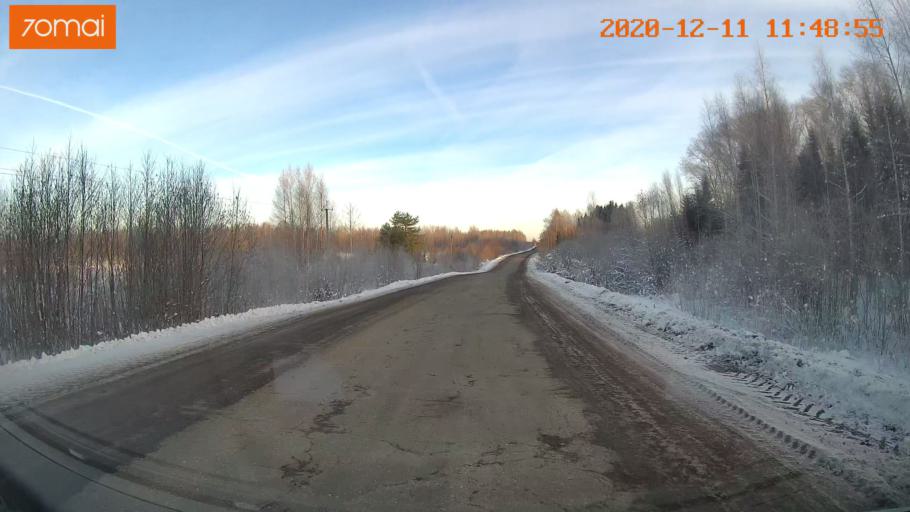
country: RU
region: Kostroma
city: Buy
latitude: 58.4532
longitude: 41.3636
